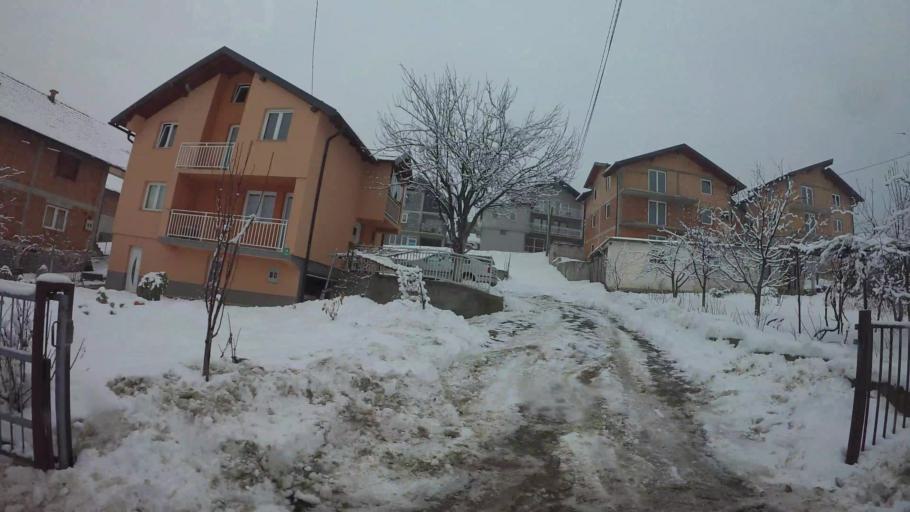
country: BA
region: Federation of Bosnia and Herzegovina
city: Vogosca
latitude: 43.8776
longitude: 18.3195
